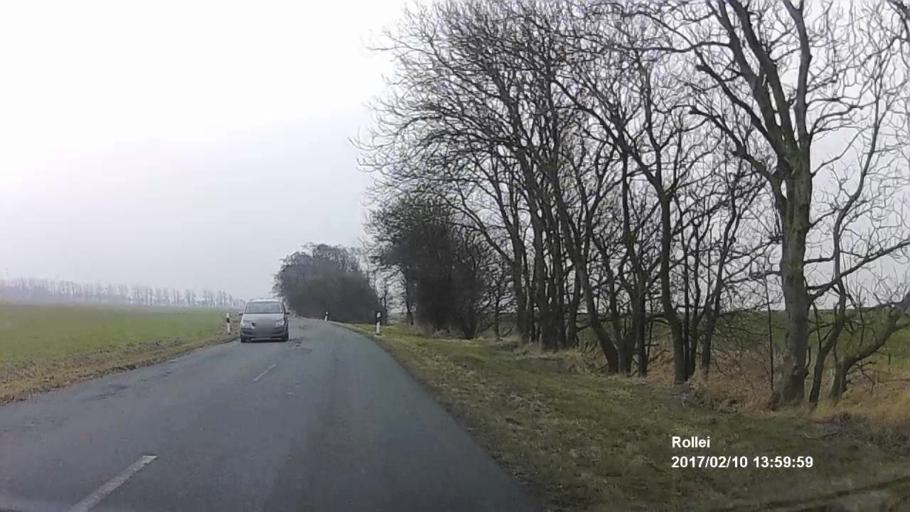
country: DE
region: Lower Saxony
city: Wirdum
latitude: 53.5246
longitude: 7.1414
